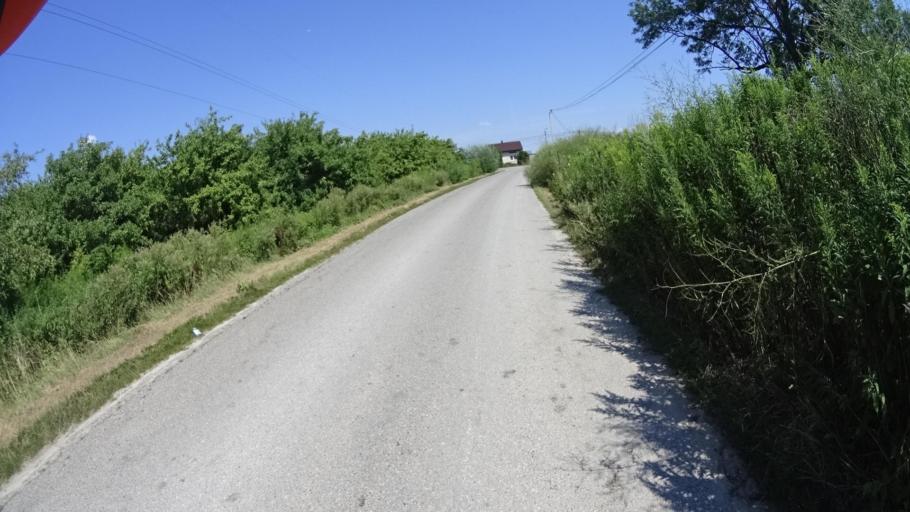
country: PL
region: Masovian Voivodeship
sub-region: Powiat piaseczynski
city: Tarczyn
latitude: 51.9783
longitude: 20.8540
